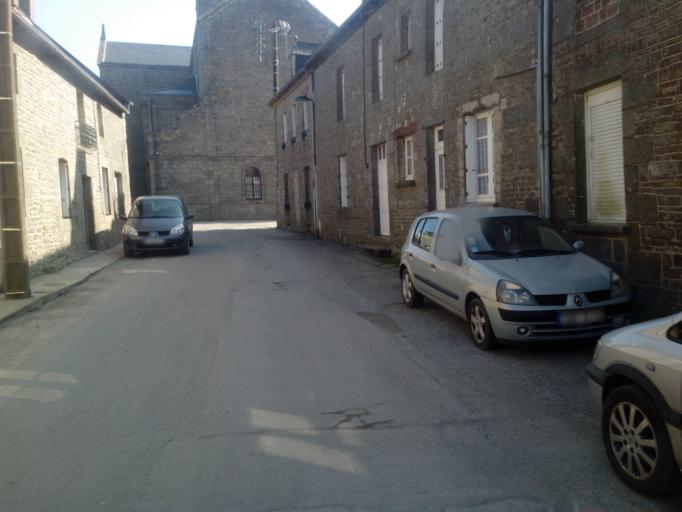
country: FR
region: Brittany
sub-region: Departement du Morbihan
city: Meneac
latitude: 48.1400
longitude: -2.4627
